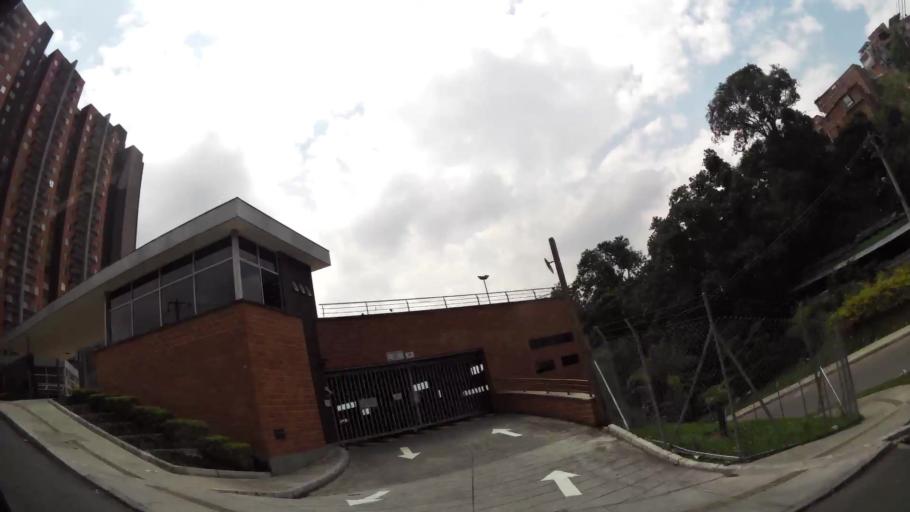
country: CO
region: Antioquia
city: Itagui
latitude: 6.1955
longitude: -75.6009
